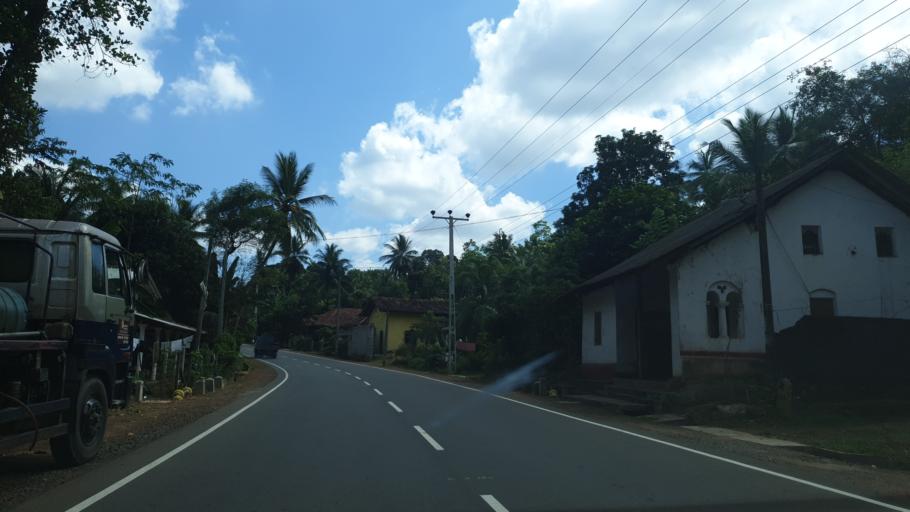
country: LK
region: Western
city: Panadura
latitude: 6.6661
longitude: 79.9628
